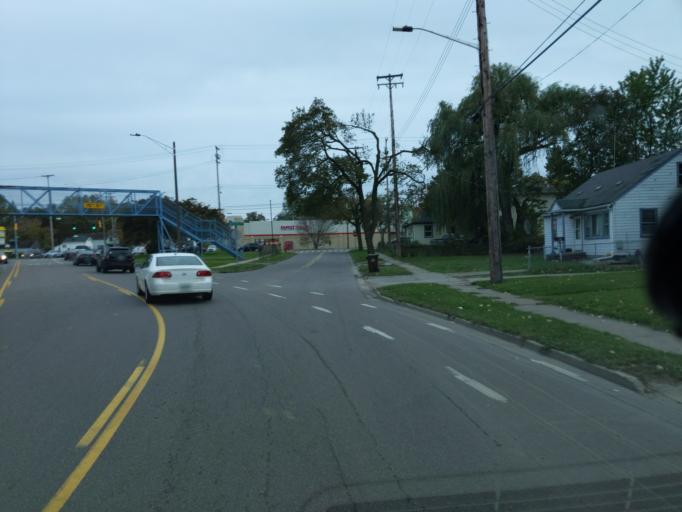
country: US
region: Michigan
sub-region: Ingham County
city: Lansing
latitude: 42.7491
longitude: -84.5680
